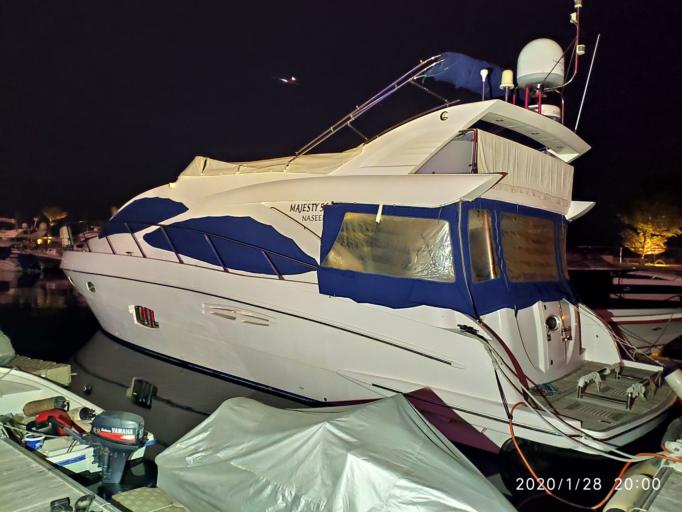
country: QA
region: Baladiyat ad Dawhah
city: Doha
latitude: 25.3243
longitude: 51.5416
